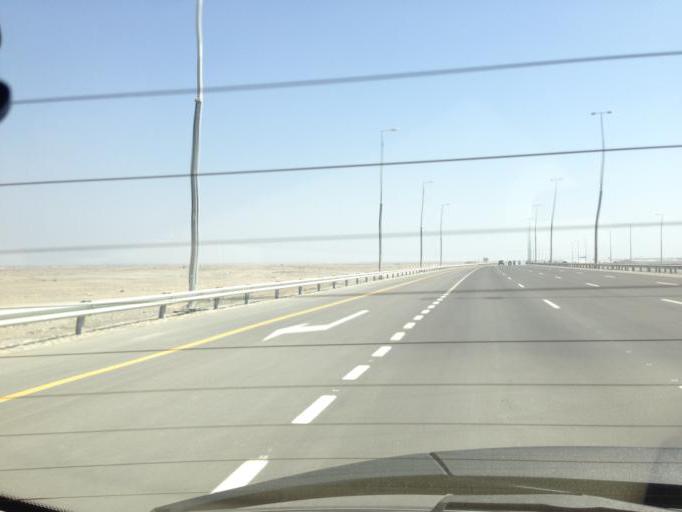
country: OM
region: Al Batinah
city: Barka'
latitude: 23.5588
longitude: 57.6943
